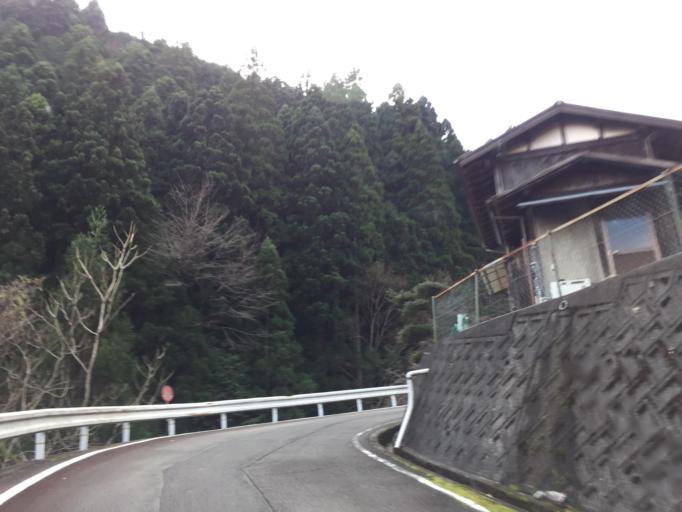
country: JP
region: Wakayama
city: Iwade
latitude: 34.1439
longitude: 135.4153
